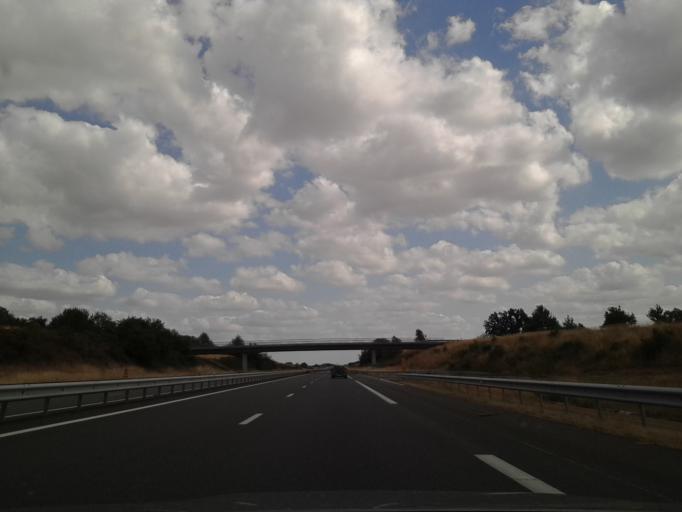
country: FR
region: Centre
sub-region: Departement du Cher
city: Saint-Amand-Montrond
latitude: 46.6298
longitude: 2.5012
